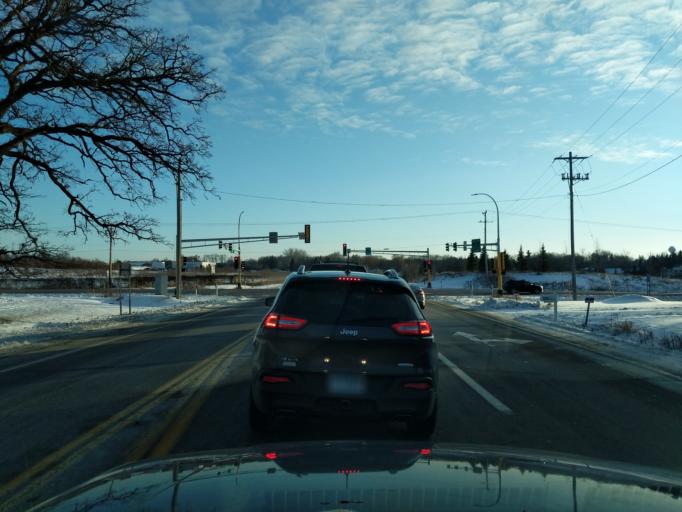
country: US
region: Minnesota
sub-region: Carver County
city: Victoria
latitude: 44.8677
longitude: -93.6371
